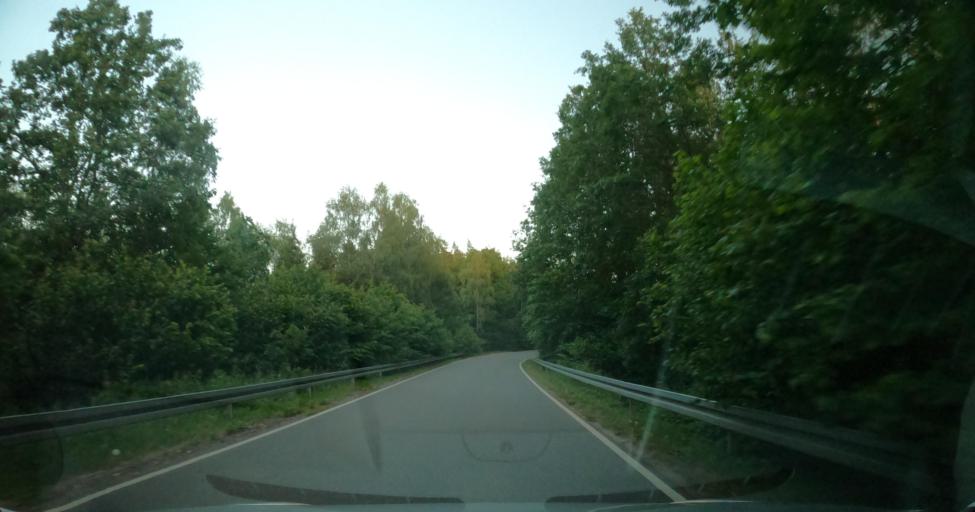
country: PL
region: Pomeranian Voivodeship
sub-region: Powiat leborski
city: Lebork
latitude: 54.5106
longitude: 17.8100
